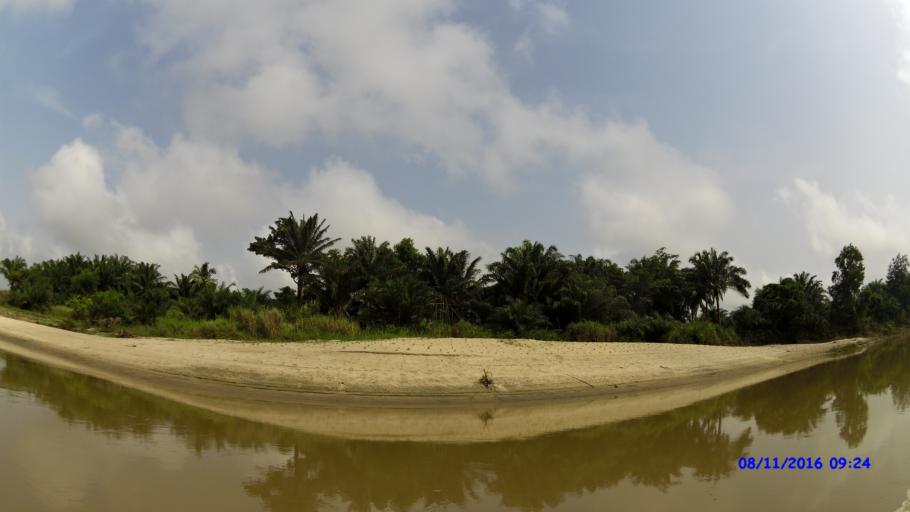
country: BJ
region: Mono
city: Come
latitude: 6.4058
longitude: 1.7661
